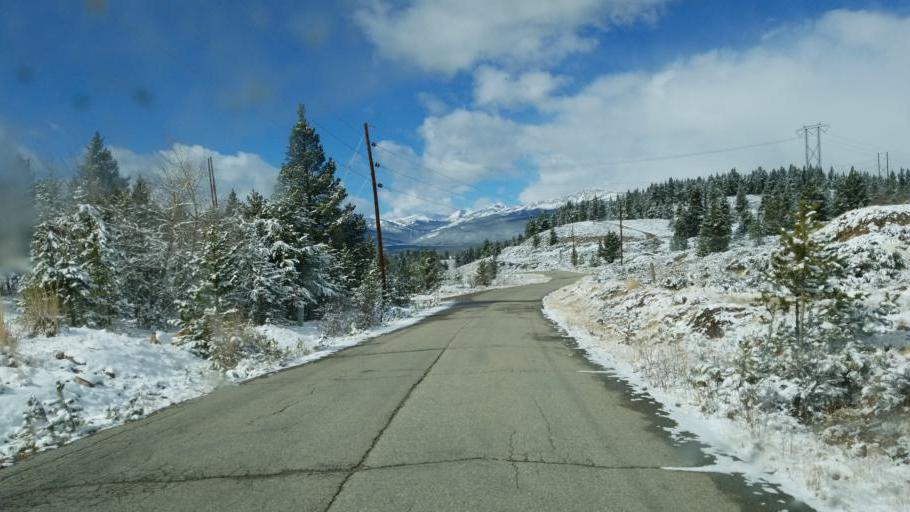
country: US
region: Colorado
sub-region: Lake County
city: Leadville
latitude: 39.2523
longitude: -106.2752
